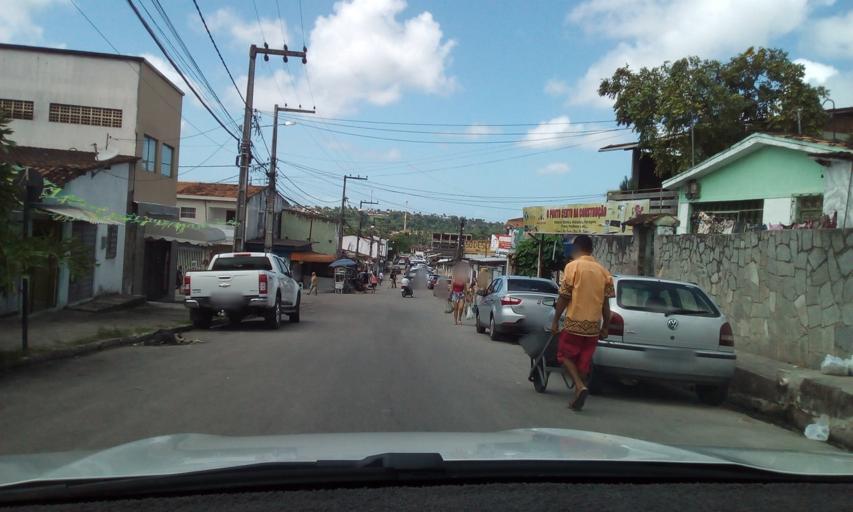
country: BR
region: Paraiba
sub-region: Bayeux
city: Bayeux
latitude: -7.1297
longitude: -34.9287
